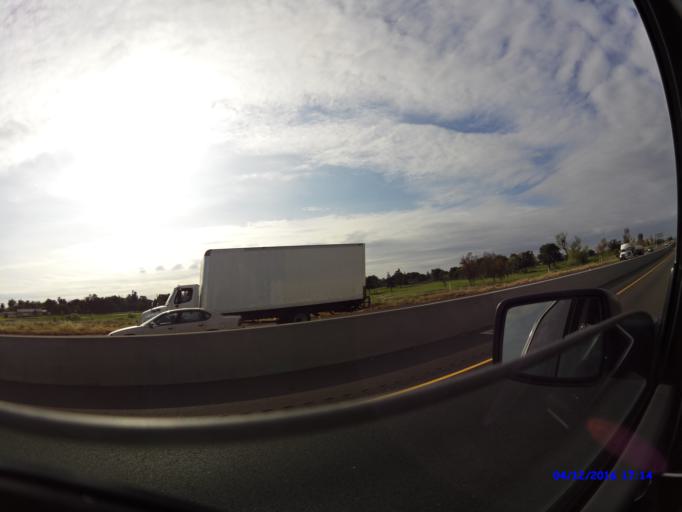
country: US
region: California
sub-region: San Joaquin County
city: French Camp
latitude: 37.8633
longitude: -121.2187
